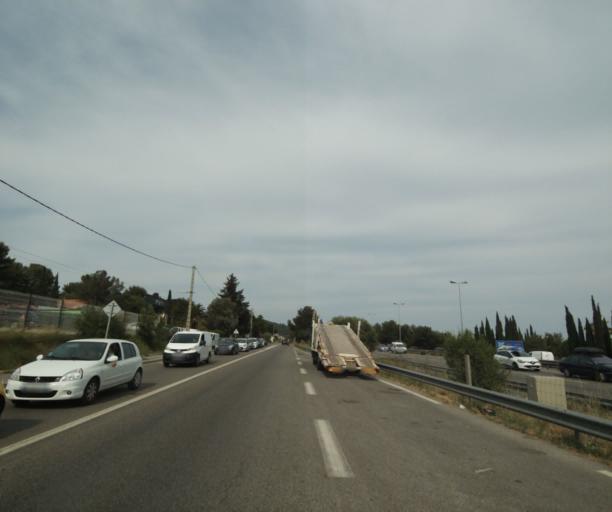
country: FR
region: Provence-Alpes-Cote d'Azur
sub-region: Departement du Var
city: La Garde
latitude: 43.1419
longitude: 6.0049
